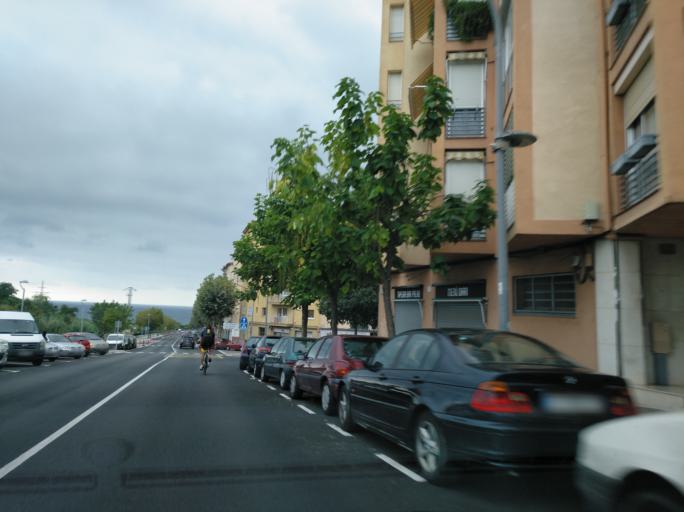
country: ES
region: Catalonia
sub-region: Provincia de Barcelona
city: Mataro
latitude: 41.5472
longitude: 2.4537
